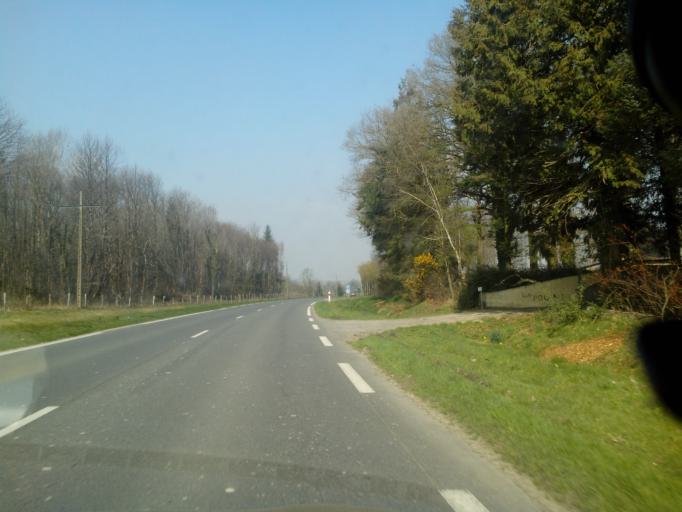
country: FR
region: Brittany
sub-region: Departement d'Ille-et-Vilaine
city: Saint-Meen-le-Grand
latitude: 48.2239
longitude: -2.1777
